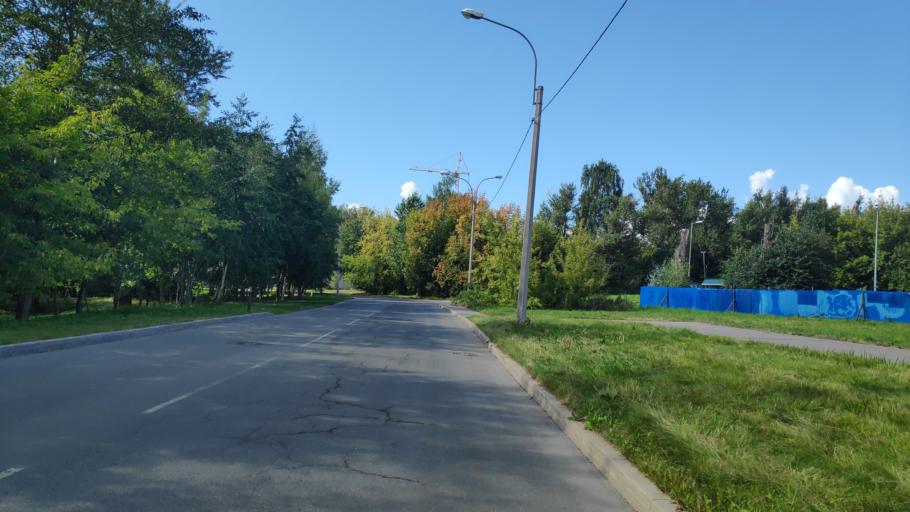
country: RU
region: St.-Petersburg
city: Krasnogvargeisky
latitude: 59.9338
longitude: 30.4258
